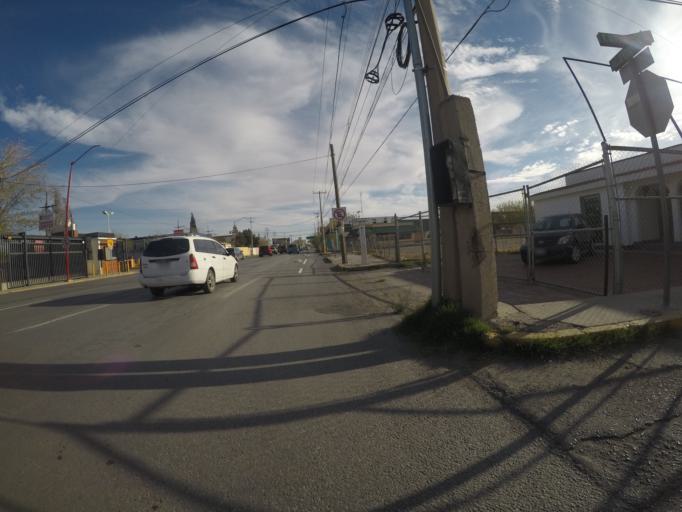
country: MX
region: Chihuahua
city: Ciudad Juarez
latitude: 31.7446
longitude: -106.4489
